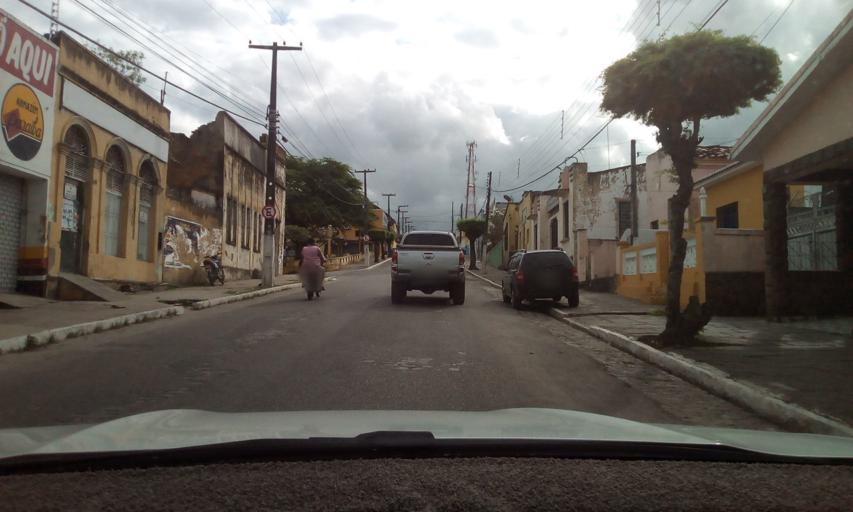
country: BR
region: Paraiba
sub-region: Mamanguape
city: Mamanguape
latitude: -6.8355
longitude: -35.1226
